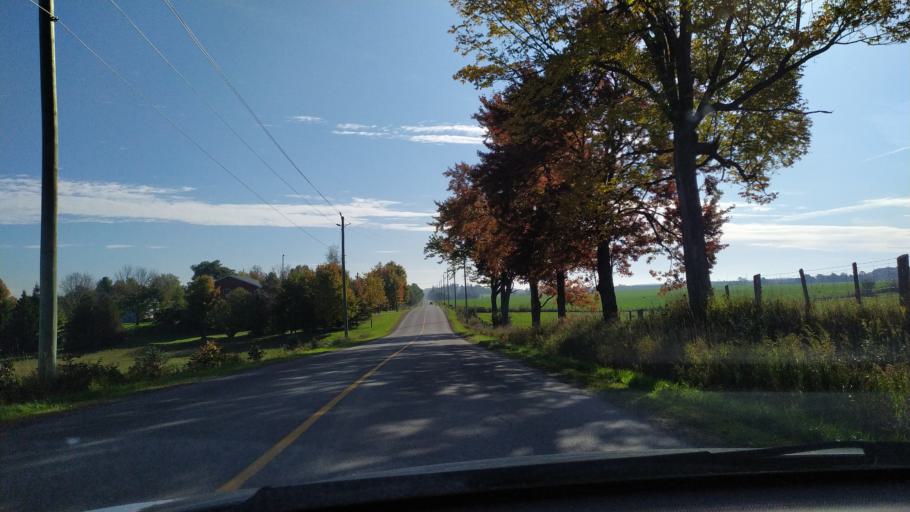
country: CA
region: Ontario
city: Waterloo
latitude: 43.4906
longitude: -80.7056
